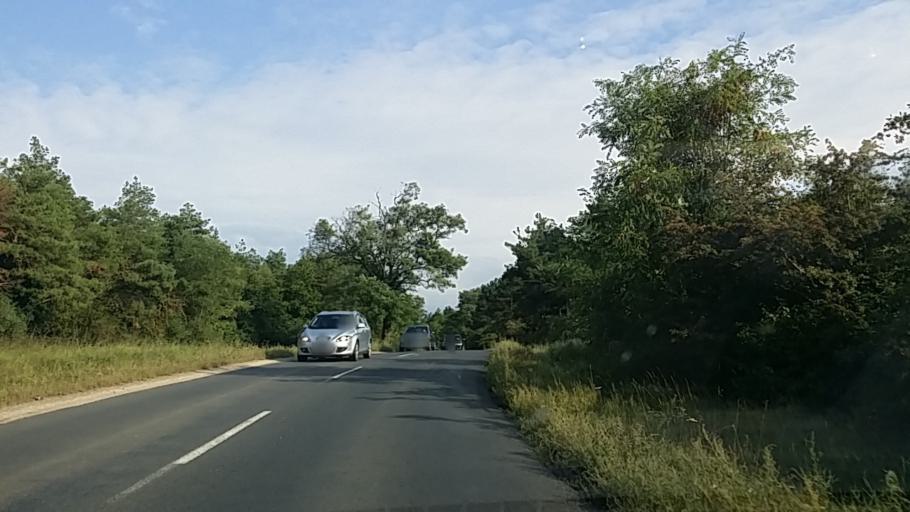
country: HU
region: Gyor-Moson-Sopron
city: Sopron
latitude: 47.6777
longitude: 16.6238
